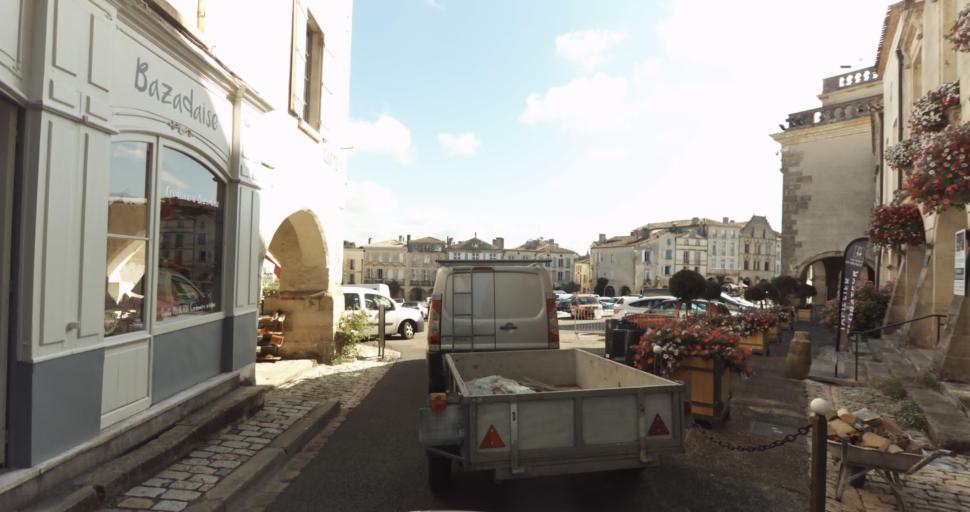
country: FR
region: Aquitaine
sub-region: Departement de la Gironde
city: Bazas
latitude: 44.4311
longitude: -0.2120
